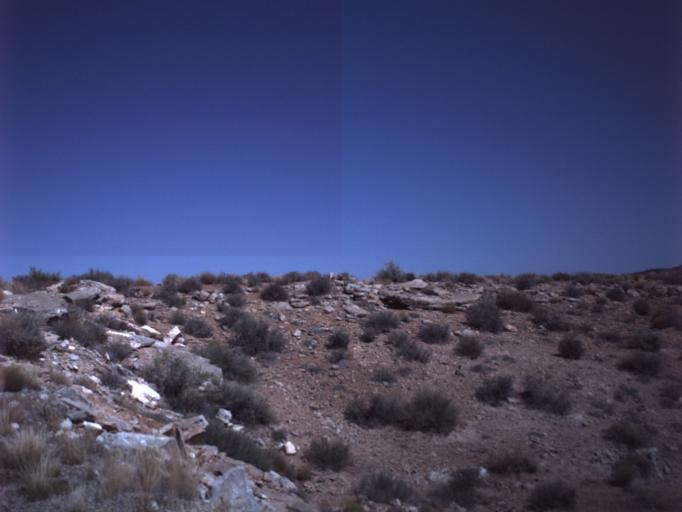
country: US
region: Arizona
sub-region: Navajo County
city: Kayenta
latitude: 37.1779
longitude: -109.9247
